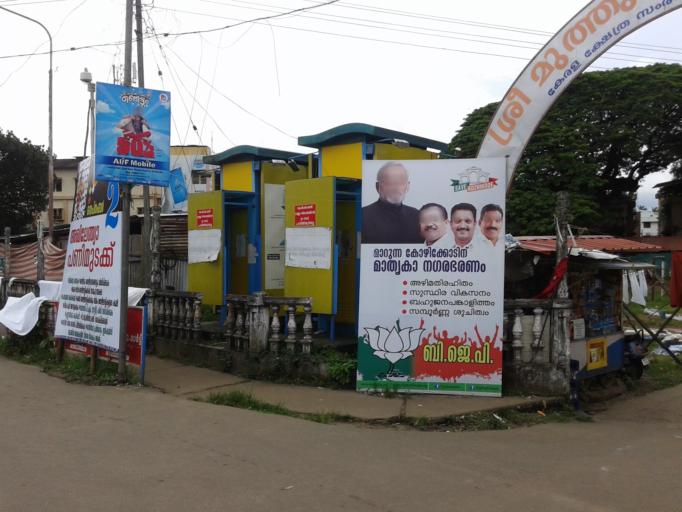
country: IN
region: Kerala
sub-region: Kozhikode
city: Kozhikode
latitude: 11.2536
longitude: 75.7832
